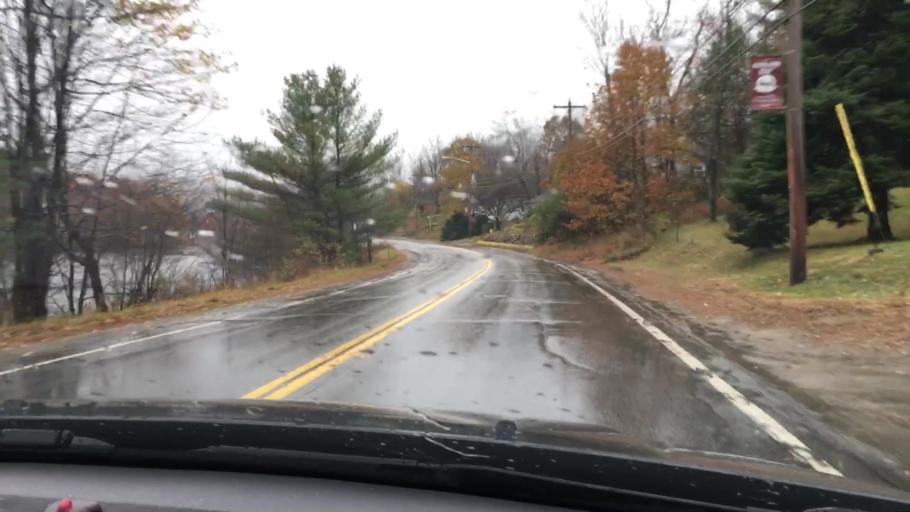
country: US
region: New Hampshire
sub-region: Grafton County
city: Ashland
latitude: 43.6988
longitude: -71.6305
